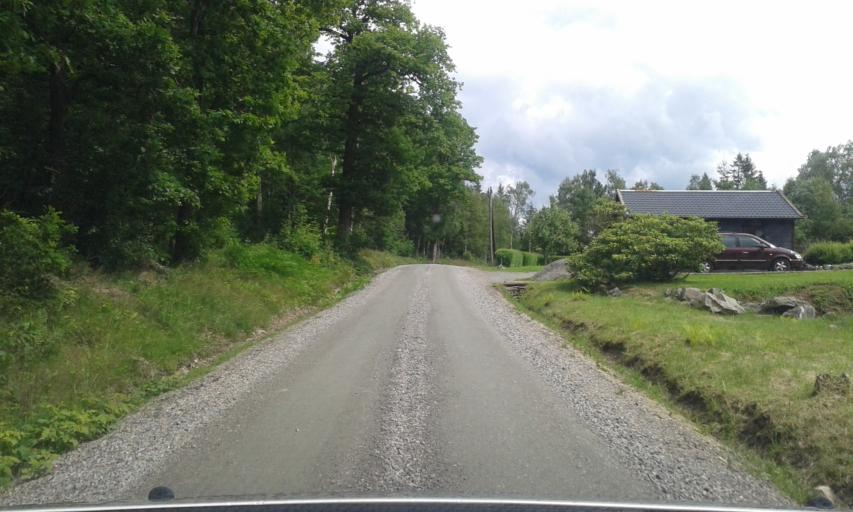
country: SE
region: Vaestra Goetaland
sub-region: Kungalvs Kommun
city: Diserod
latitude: 57.9624
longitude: 12.0141
